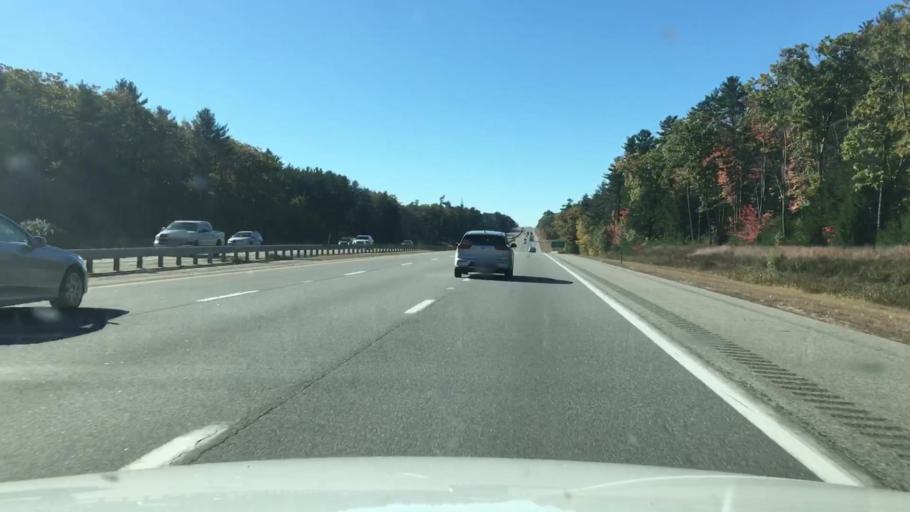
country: US
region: Maine
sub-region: York County
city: West Kennebunk
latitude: 43.3798
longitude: -70.5769
